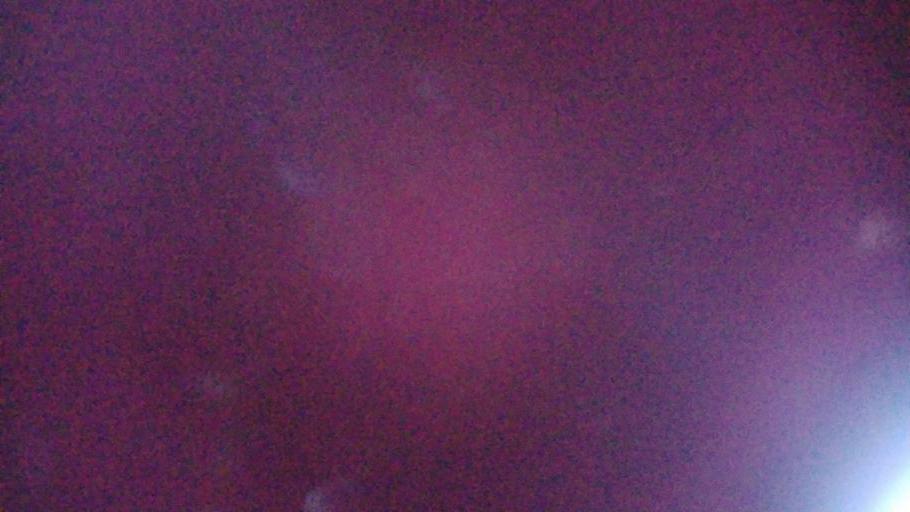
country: US
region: Florida
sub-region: Lee County
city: Olga
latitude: 26.7782
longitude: -81.7411
